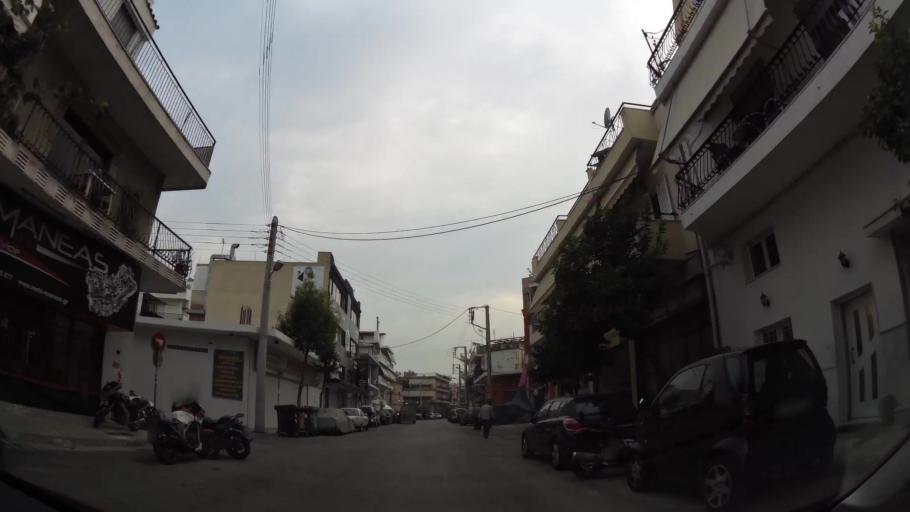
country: GR
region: Attica
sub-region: Nomarchia Athinas
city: Peristeri
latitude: 38.0053
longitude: 23.6966
